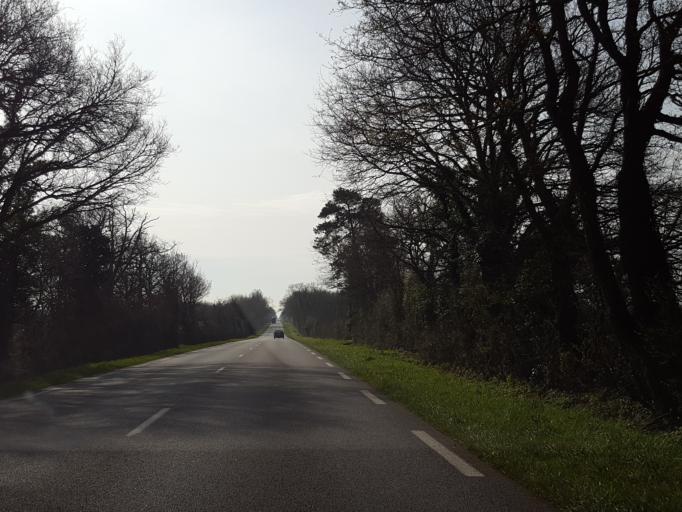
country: FR
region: Pays de la Loire
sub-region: Departement de la Vendee
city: Les Lucs-sur-Boulogne
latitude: 46.8299
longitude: -1.4801
